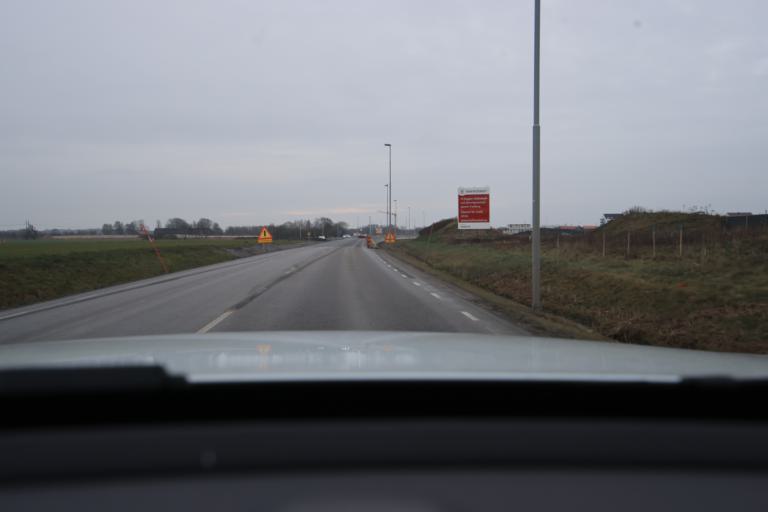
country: SE
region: Halland
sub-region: Varbergs Kommun
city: Traslovslage
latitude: 57.0913
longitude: 12.2927
